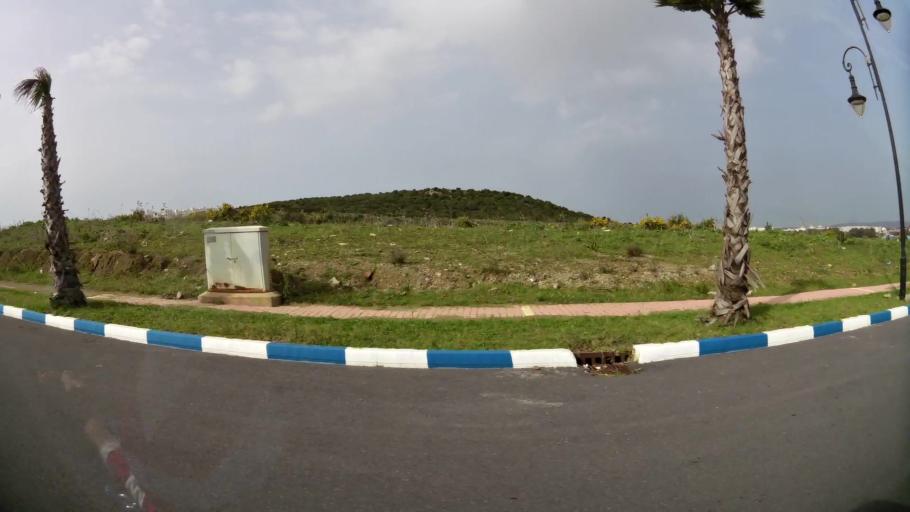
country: MA
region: Tanger-Tetouan
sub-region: Tanger-Assilah
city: Boukhalef
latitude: 35.6977
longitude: -5.9274
